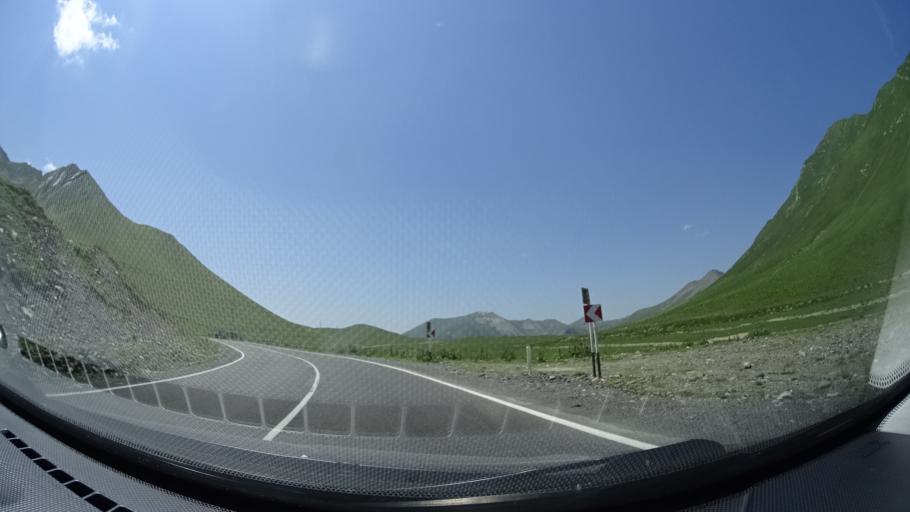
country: GE
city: Gudauri
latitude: 42.5146
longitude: 44.4623
